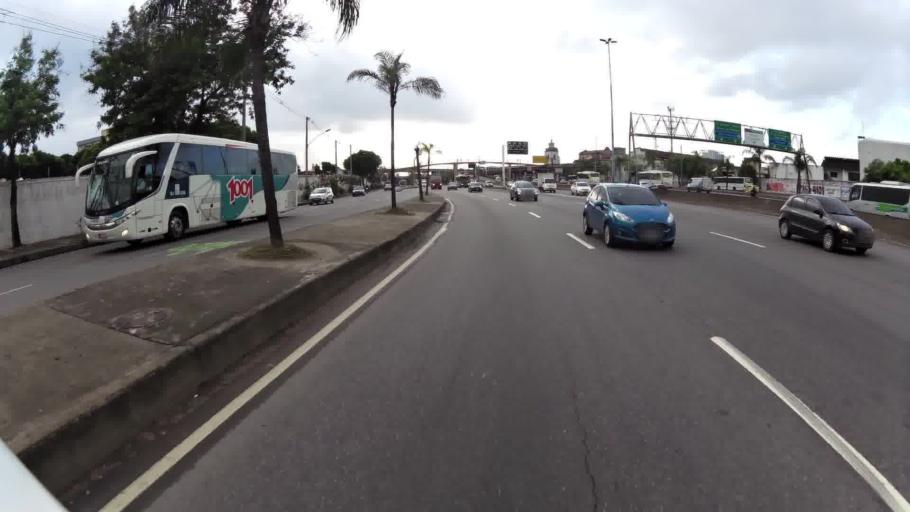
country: BR
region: Rio de Janeiro
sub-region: Rio De Janeiro
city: Rio de Janeiro
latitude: -22.8887
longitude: -43.2222
